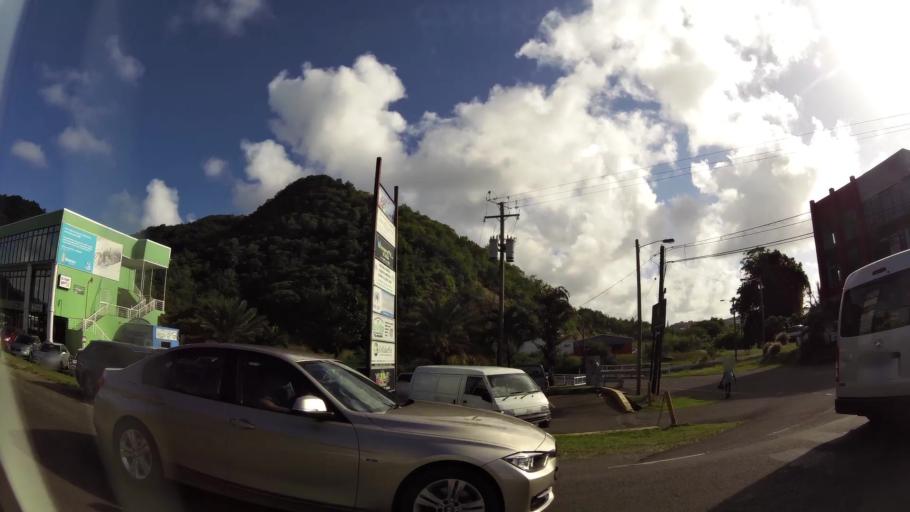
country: LC
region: Gros-Islet
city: Gros Islet
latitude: 14.0545
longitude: -60.9632
